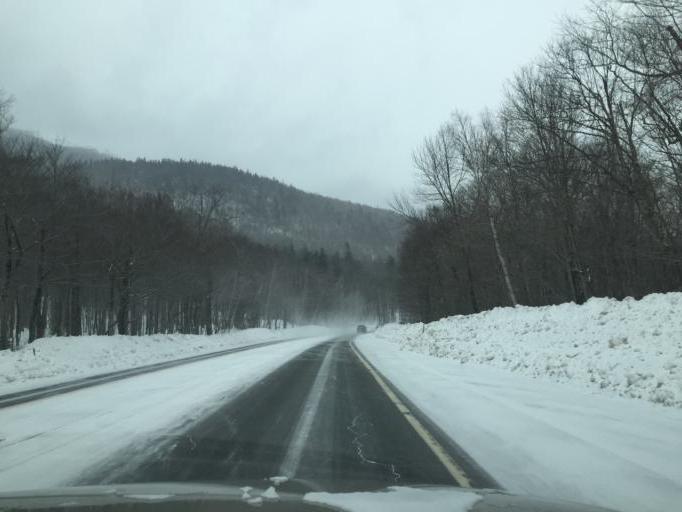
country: US
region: New Hampshire
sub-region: Coos County
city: Gorham
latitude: 44.2315
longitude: -71.2554
